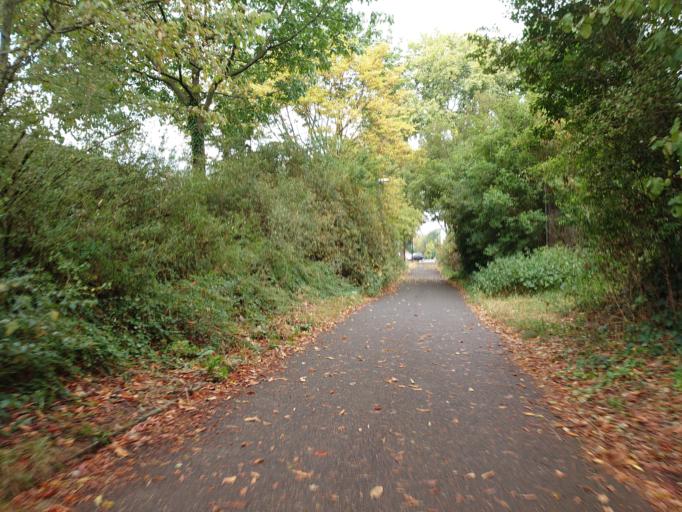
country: DE
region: North Rhine-Westphalia
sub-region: Regierungsbezirk Koln
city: Nippes
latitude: 50.9851
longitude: 6.9621
